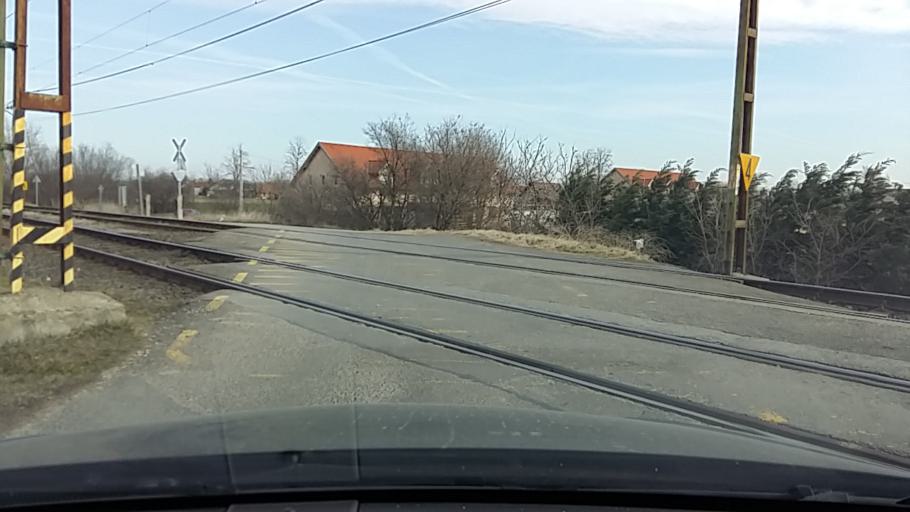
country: HU
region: Pest
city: Szigetszentmiklos
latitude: 47.3532
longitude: 19.0650
